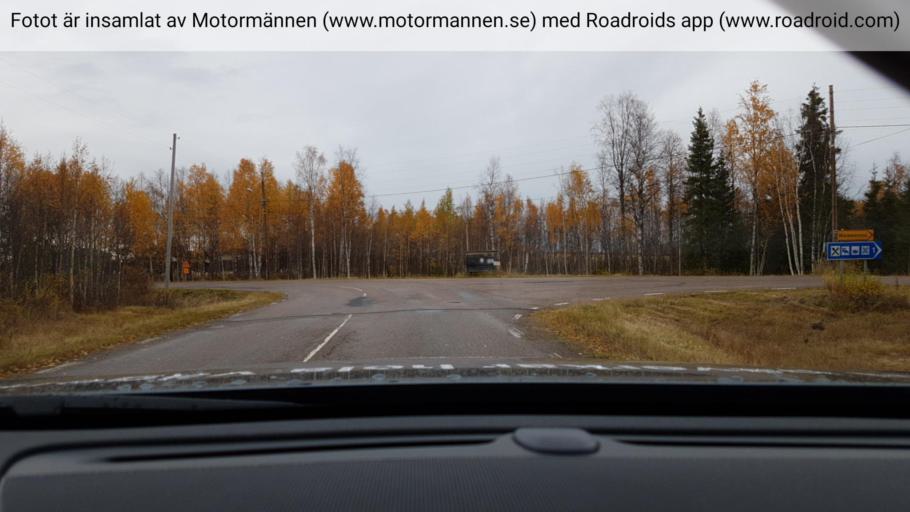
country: SE
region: Norrbotten
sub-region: Pajala Kommun
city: Pajala
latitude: 67.1757
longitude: 22.6486
